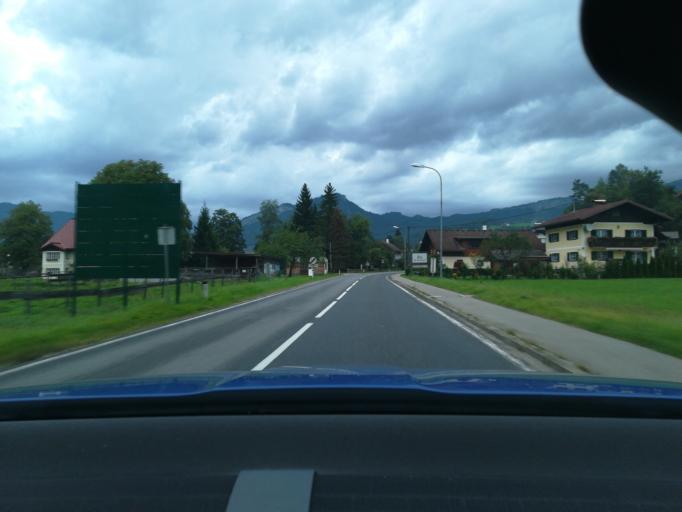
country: AT
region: Upper Austria
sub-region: Politischer Bezirk Gmunden
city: Bad Goisern
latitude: 47.6150
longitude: 13.6339
